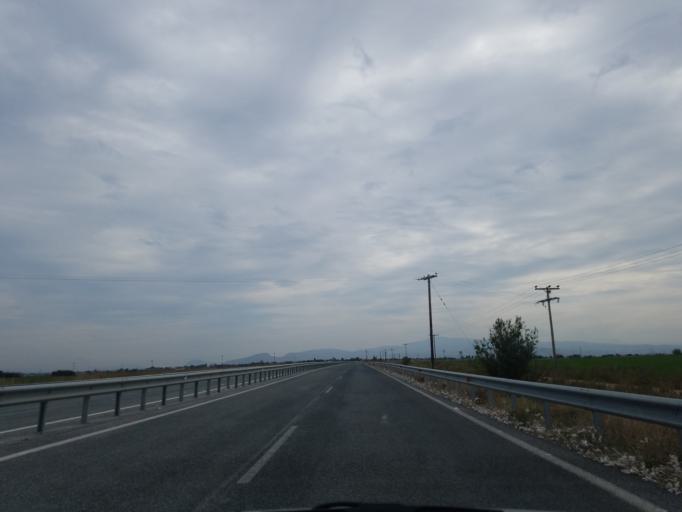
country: GR
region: Thessaly
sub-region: Nomos Kardhitsas
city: Sofades
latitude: 39.2933
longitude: 22.1716
